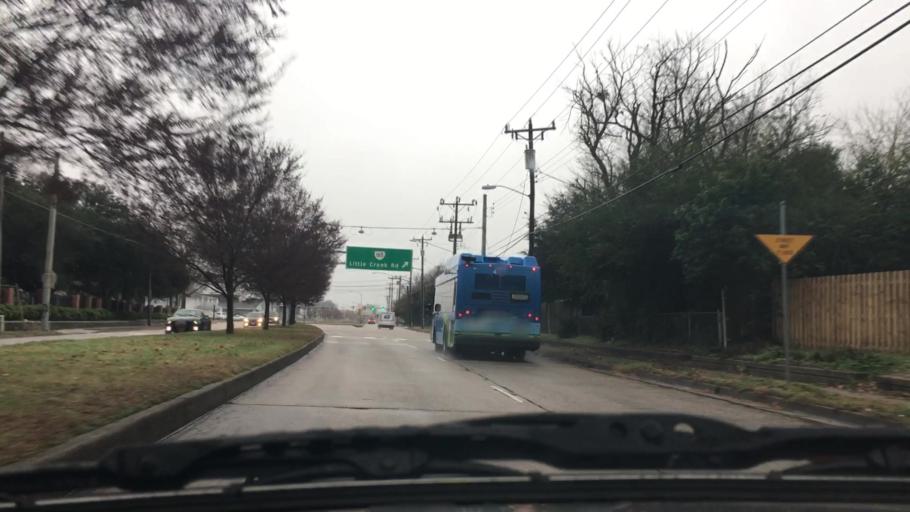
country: US
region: Virginia
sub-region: City of Norfolk
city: Norfolk
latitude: 36.9193
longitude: -76.2535
